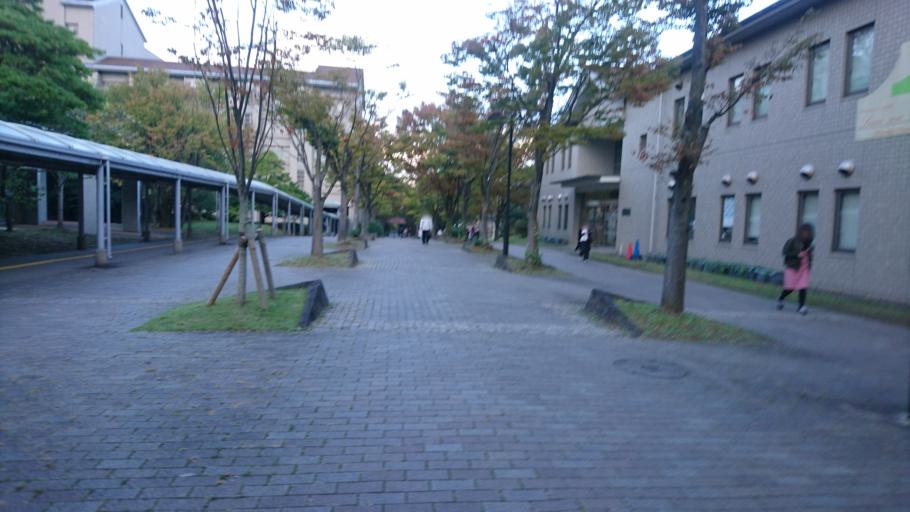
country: JP
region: Tokyo
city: Hino
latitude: 35.6192
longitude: 139.3803
